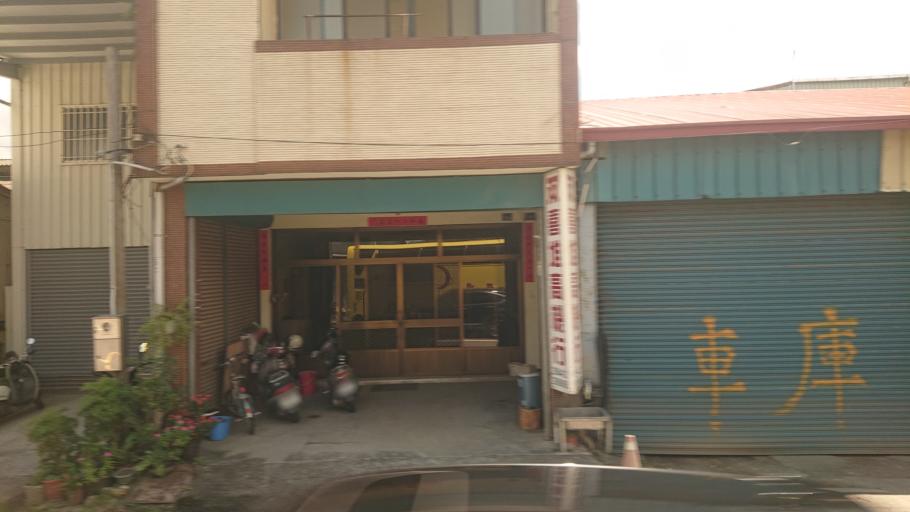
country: TW
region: Taiwan
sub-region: Nantou
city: Puli
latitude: 23.9740
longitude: 120.9627
